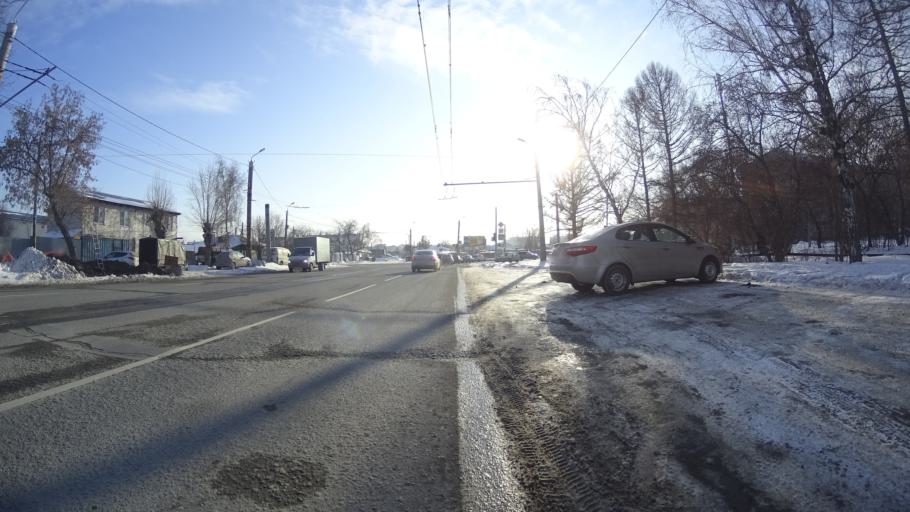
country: RU
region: Chelyabinsk
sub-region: Gorod Chelyabinsk
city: Chelyabinsk
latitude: 55.1845
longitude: 61.4589
